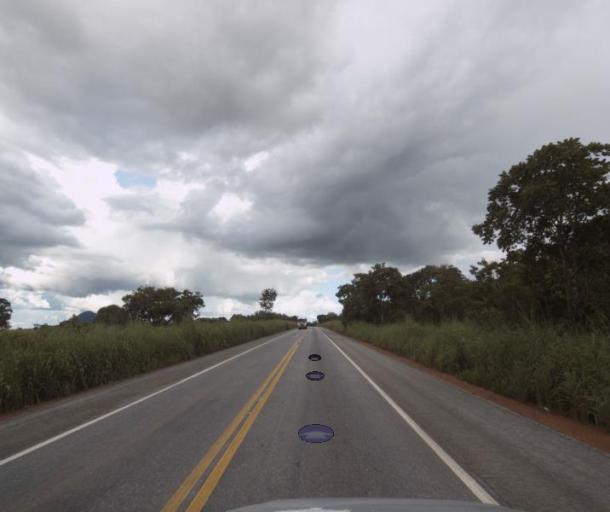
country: BR
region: Goias
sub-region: Porangatu
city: Porangatu
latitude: -13.3051
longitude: -49.1198
